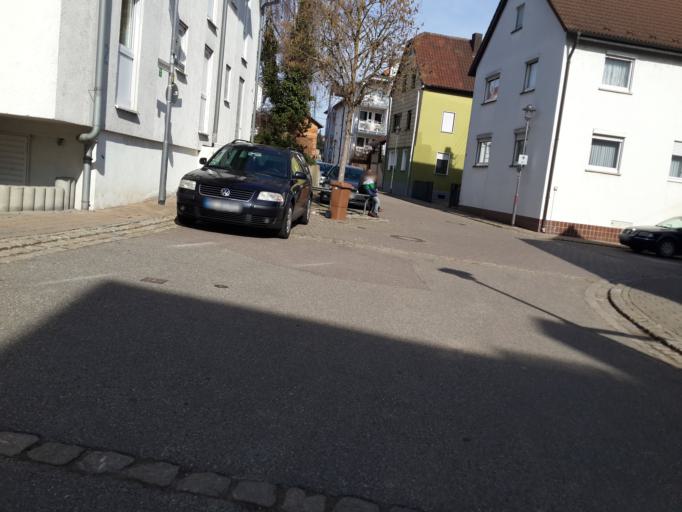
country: DE
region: Baden-Wuerttemberg
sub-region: Regierungsbezirk Stuttgart
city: Heilbronn
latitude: 49.1579
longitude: 9.1700
